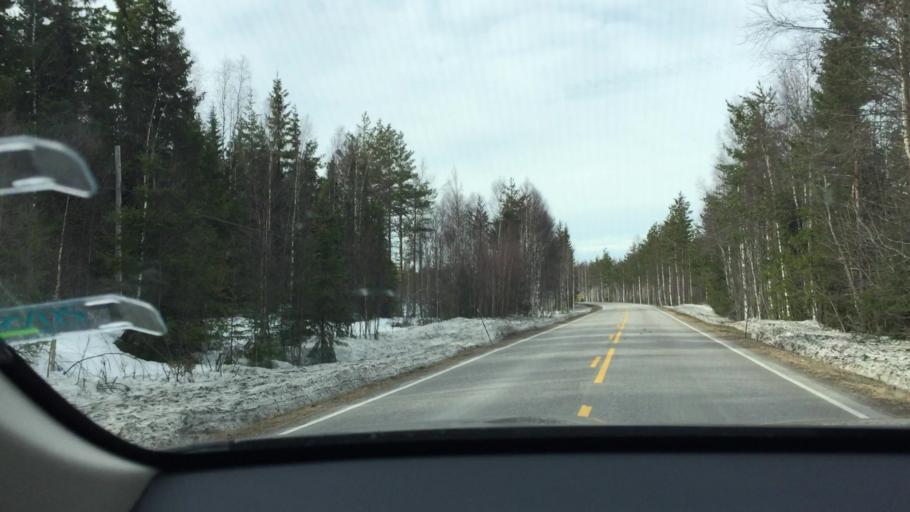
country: NO
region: Hedmark
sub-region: Trysil
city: Innbygda
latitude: 61.0711
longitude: 12.5785
